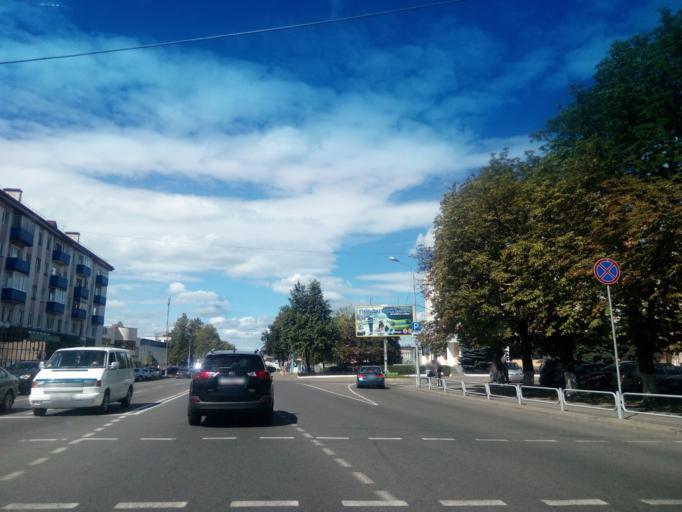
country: BY
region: Vitebsk
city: Polatsk
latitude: 55.4909
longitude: 28.7803
